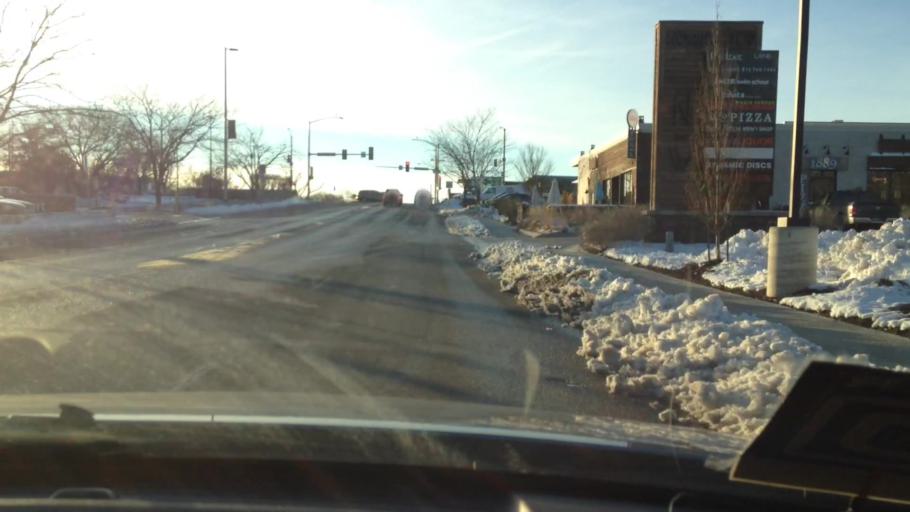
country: US
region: Kansas
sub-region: Johnson County
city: Westwood
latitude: 39.0441
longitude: -94.6196
